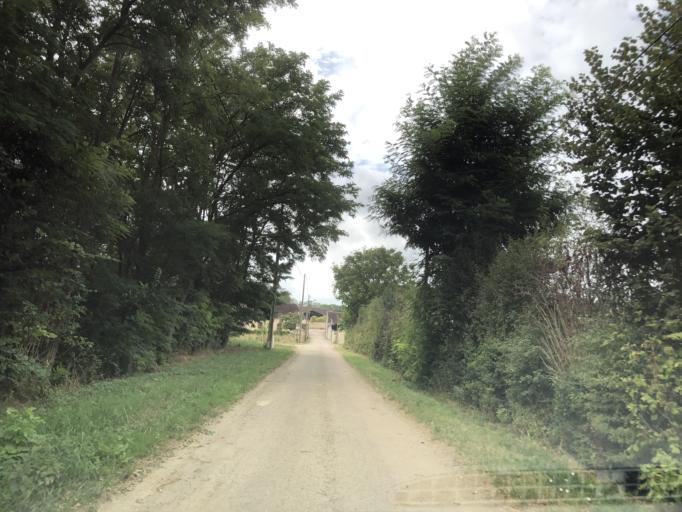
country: FR
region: Bourgogne
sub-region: Departement de l'Yonne
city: Laroche-Saint-Cydroine
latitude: 47.9475
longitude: 3.4480
